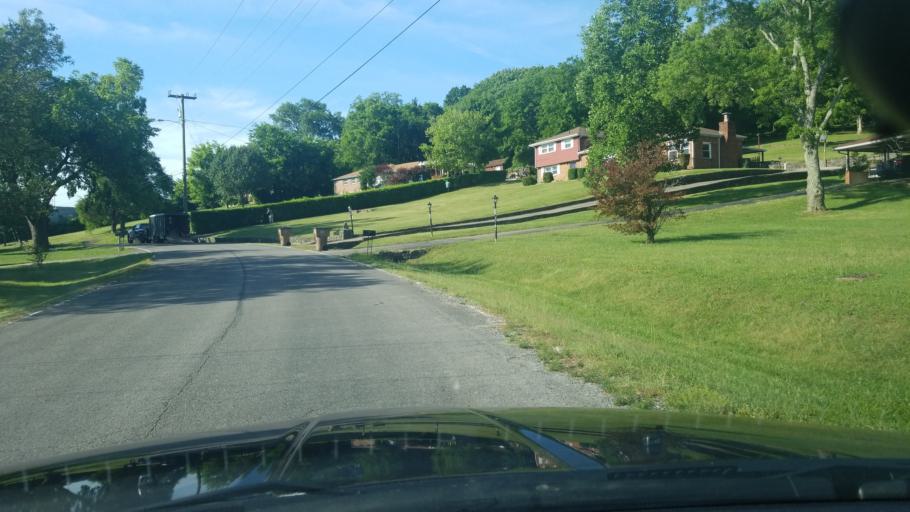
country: US
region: Tennessee
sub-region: Davidson County
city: Nashville
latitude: 36.2299
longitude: -86.7739
